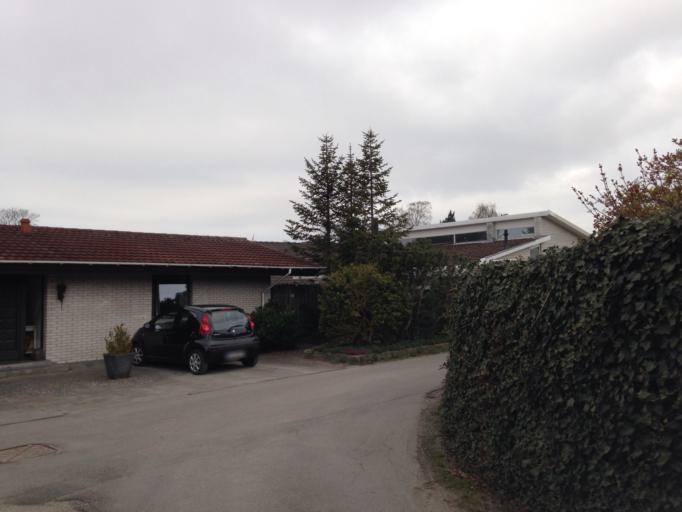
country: DK
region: Zealand
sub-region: Greve Kommune
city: Greve
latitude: 55.5703
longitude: 12.2866
